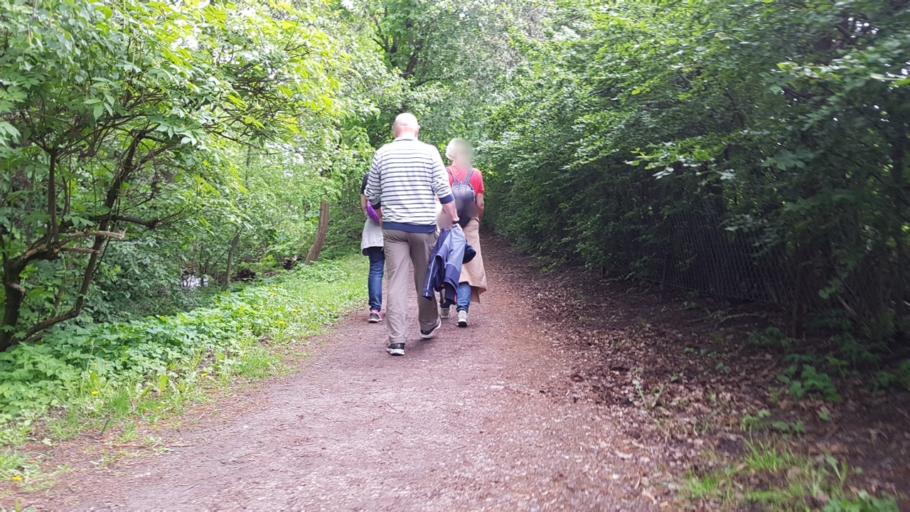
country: NO
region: Oslo
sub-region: Oslo
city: Oslo
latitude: 59.9424
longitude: 10.8205
